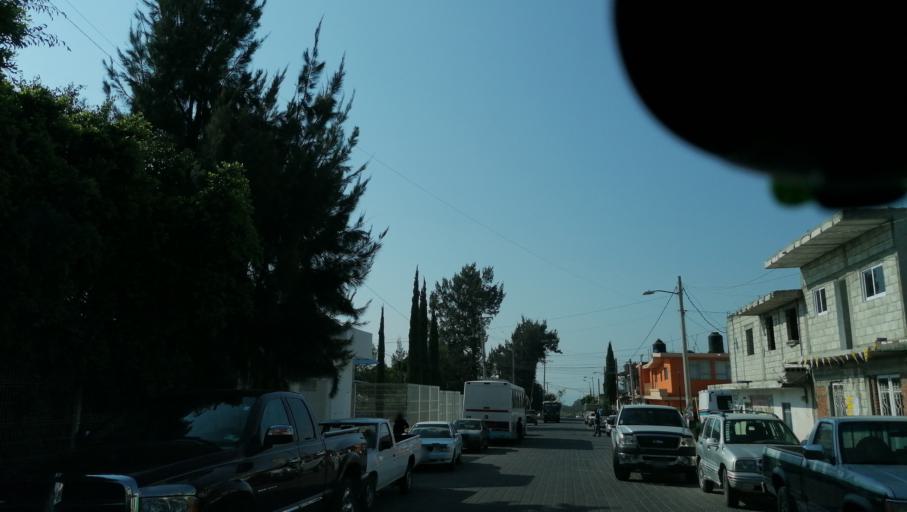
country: MX
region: Puebla
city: San Juan Tianguismanalco
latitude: 18.9314
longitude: -98.4575
